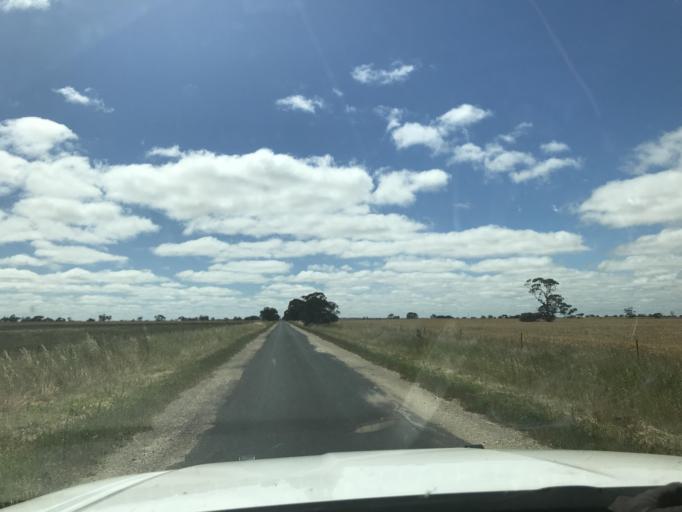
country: AU
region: South Australia
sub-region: Tatiara
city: Bordertown
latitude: -36.2807
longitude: 141.1376
